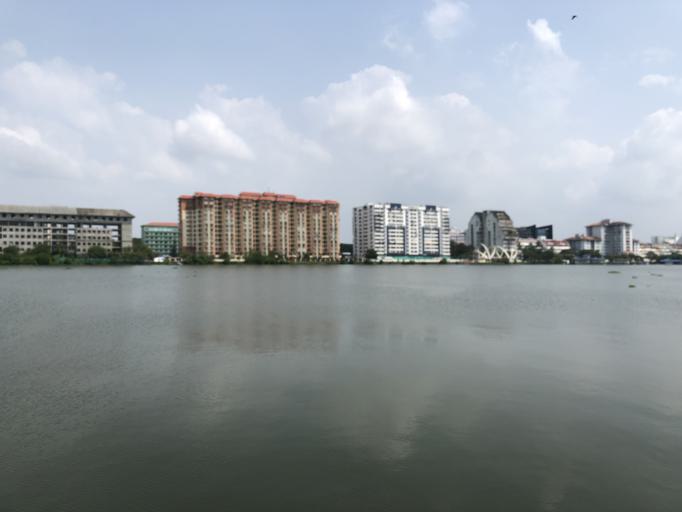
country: IN
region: Kerala
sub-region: Ernakulam
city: Cochin
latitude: 9.9874
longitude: 76.2678
